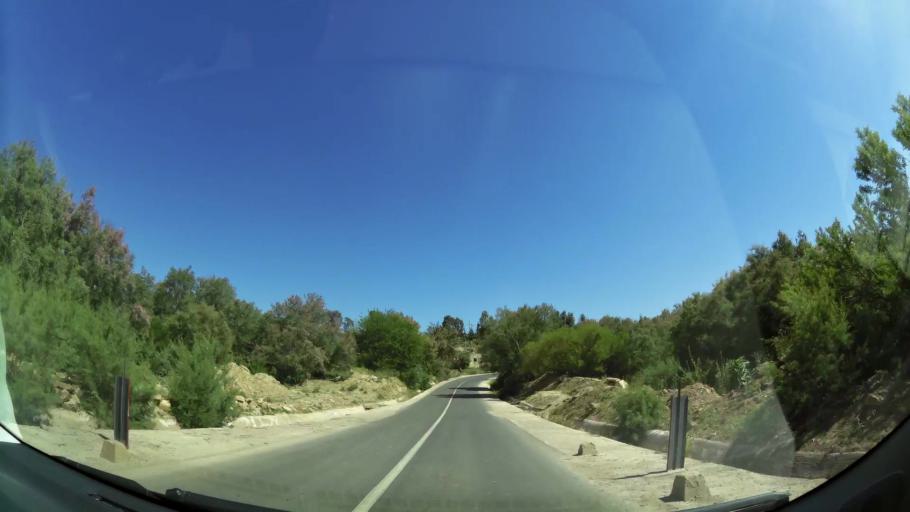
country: MA
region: Oriental
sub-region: Berkane-Taourirt
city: Madagh
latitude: 35.0512
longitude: -2.4281
